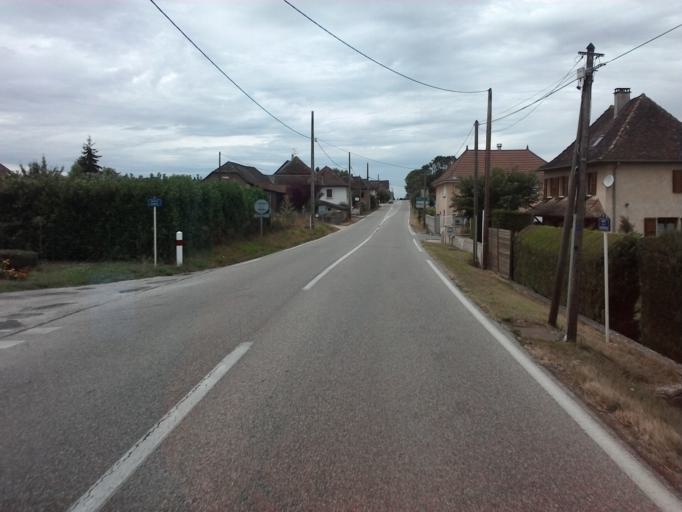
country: FR
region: Rhone-Alpes
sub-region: Departement de l'Isere
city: Curtin
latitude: 45.6467
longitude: 5.4916
